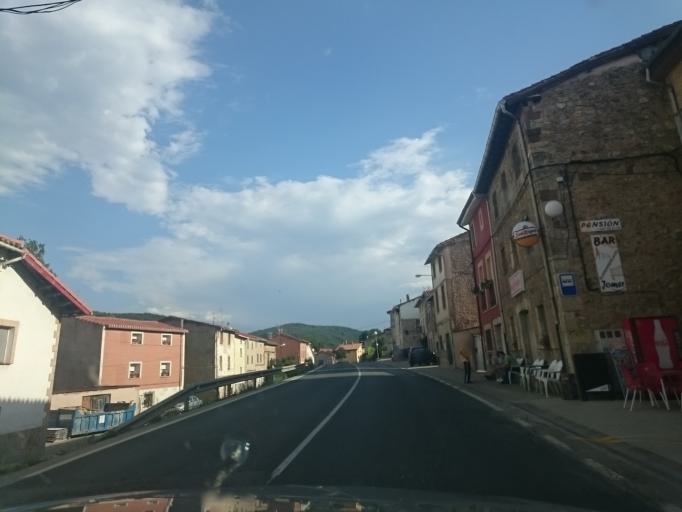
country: ES
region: Castille and Leon
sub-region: Provincia de Burgos
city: Espinosa del Camino
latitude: 42.3867
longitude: -3.3090
